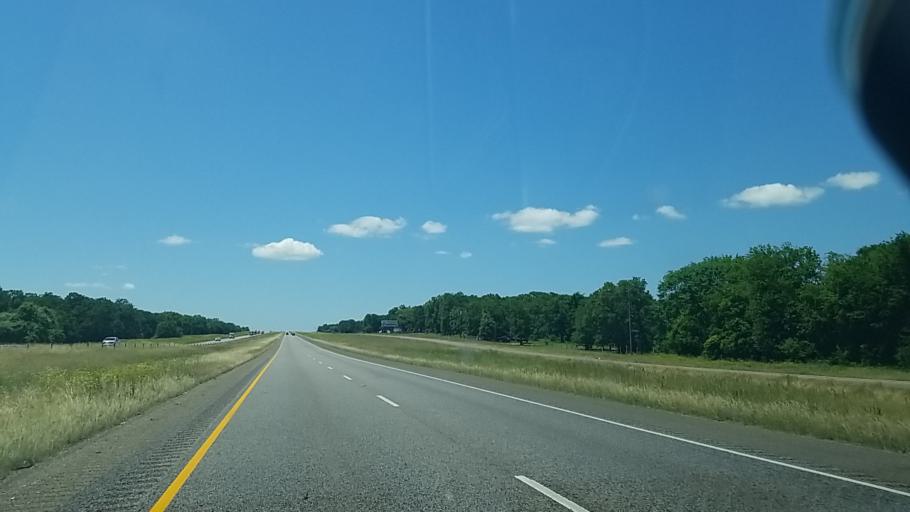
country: US
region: Texas
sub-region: Madison County
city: Madisonville
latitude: 30.9394
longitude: -95.8420
